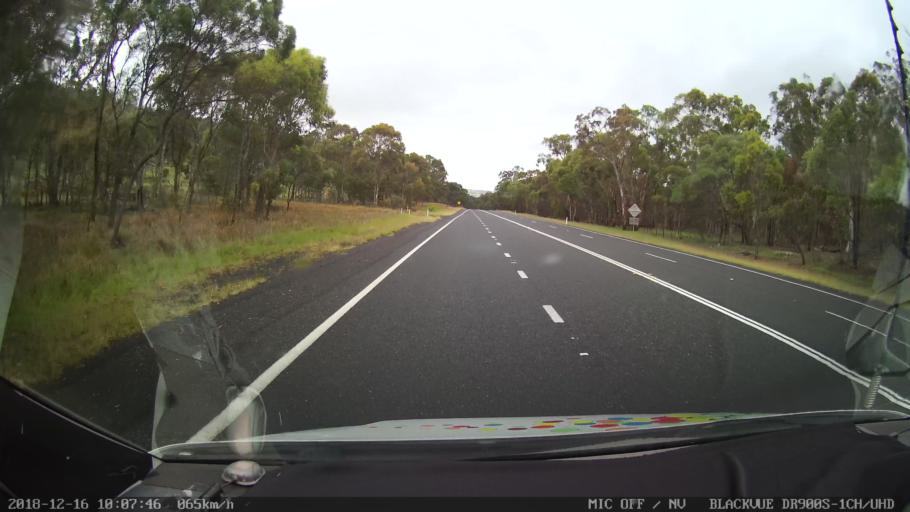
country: AU
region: New South Wales
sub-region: Glen Innes Severn
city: Glen Innes
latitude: -29.3337
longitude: 151.8991
